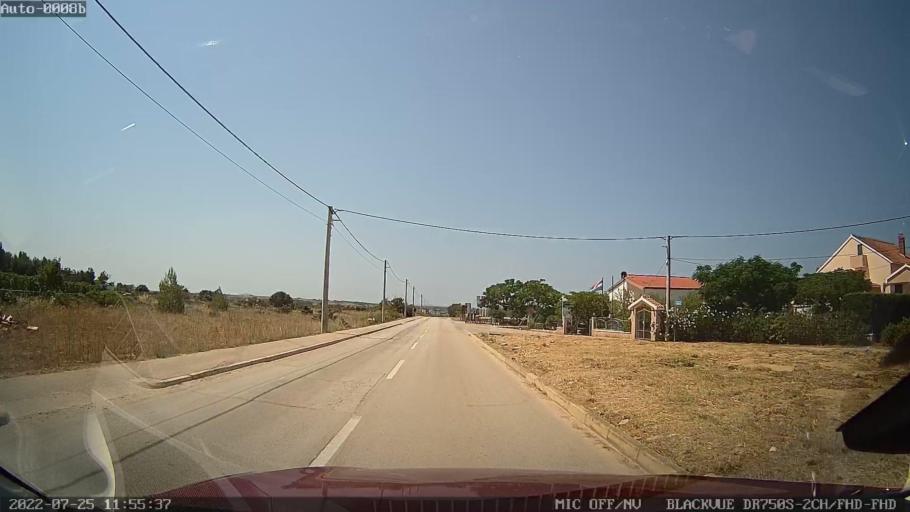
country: HR
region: Zadarska
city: Vrsi
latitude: 44.2568
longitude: 15.2232
